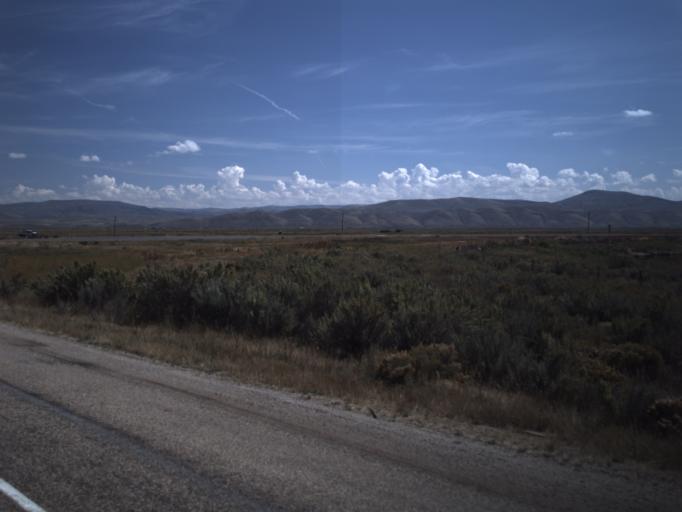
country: US
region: Utah
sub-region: Rich County
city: Randolph
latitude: 41.7722
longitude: -111.1251
